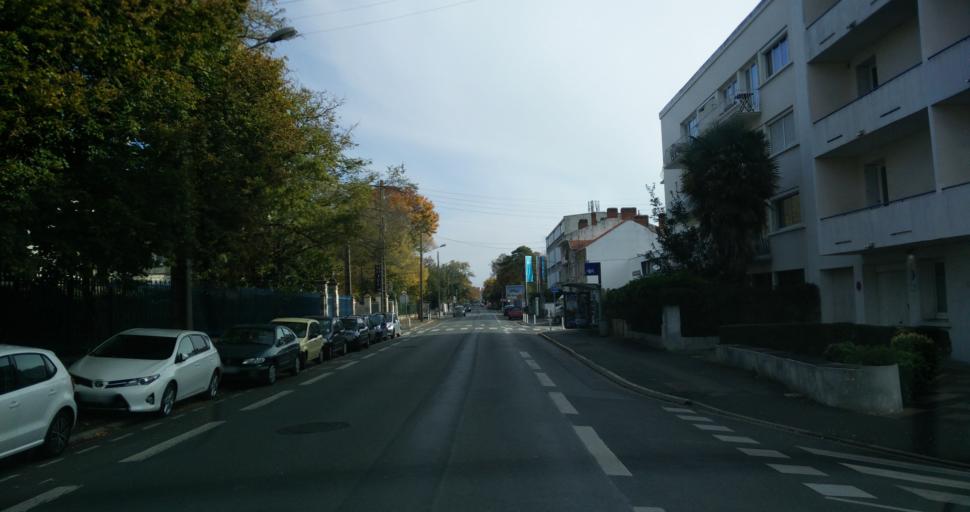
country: FR
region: Poitou-Charentes
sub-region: Departement de la Charente-Maritime
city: La Rochelle
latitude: 46.1627
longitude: -1.1616
